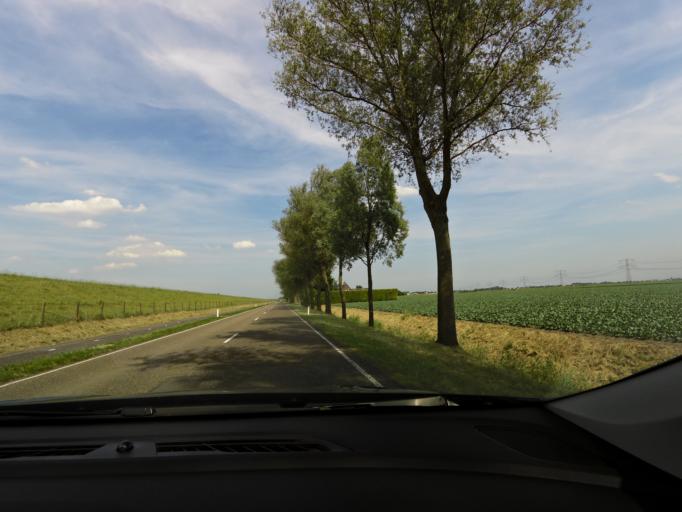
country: NL
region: South Holland
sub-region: Gemeente Spijkenisse
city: Spijkenisse
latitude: 51.8169
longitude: 4.3484
